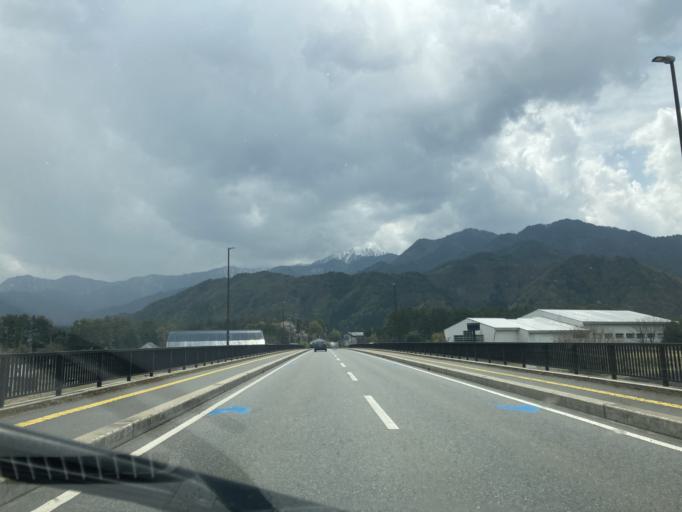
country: JP
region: Nagano
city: Omachi
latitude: 36.4981
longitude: 137.8426
